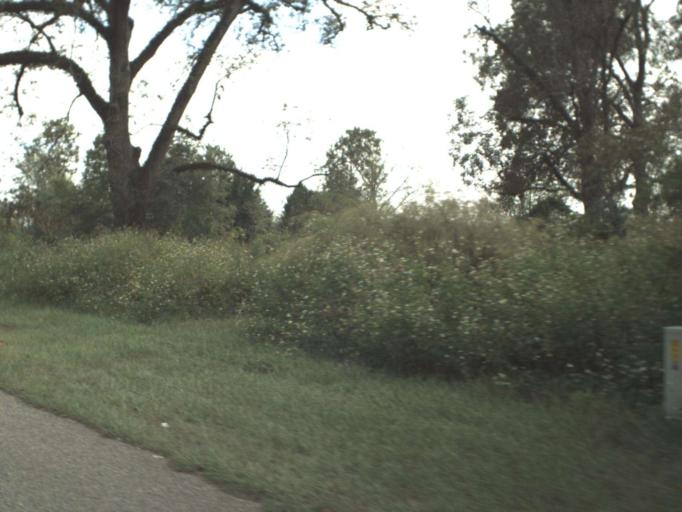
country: US
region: Florida
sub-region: Jackson County
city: Marianna
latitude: 30.6054
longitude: -85.1434
